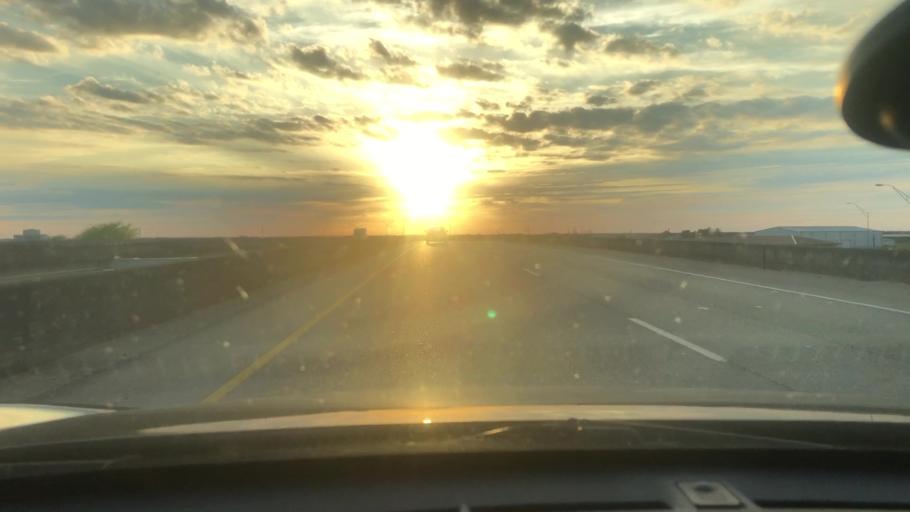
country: US
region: Texas
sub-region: Wharton County
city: El Campo
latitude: 29.1743
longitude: -96.3026
